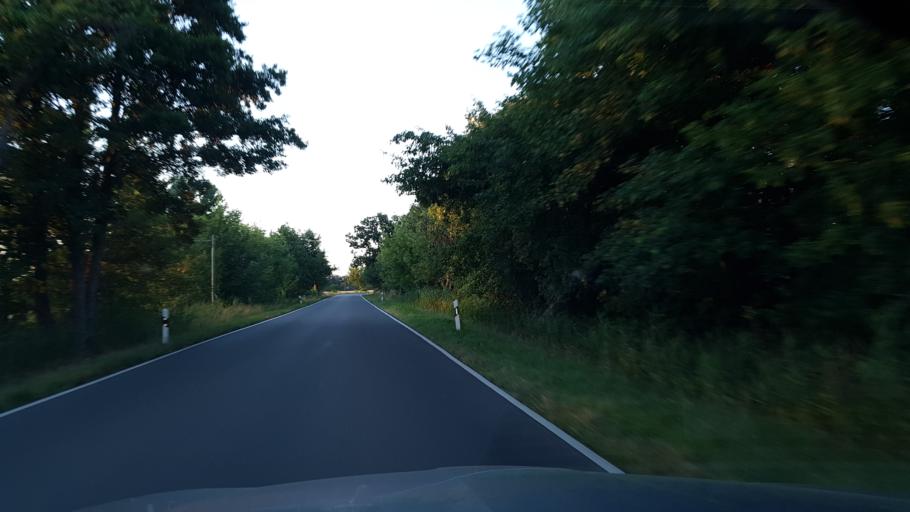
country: DE
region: Brandenburg
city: Groden
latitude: 51.4106
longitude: 13.5894
